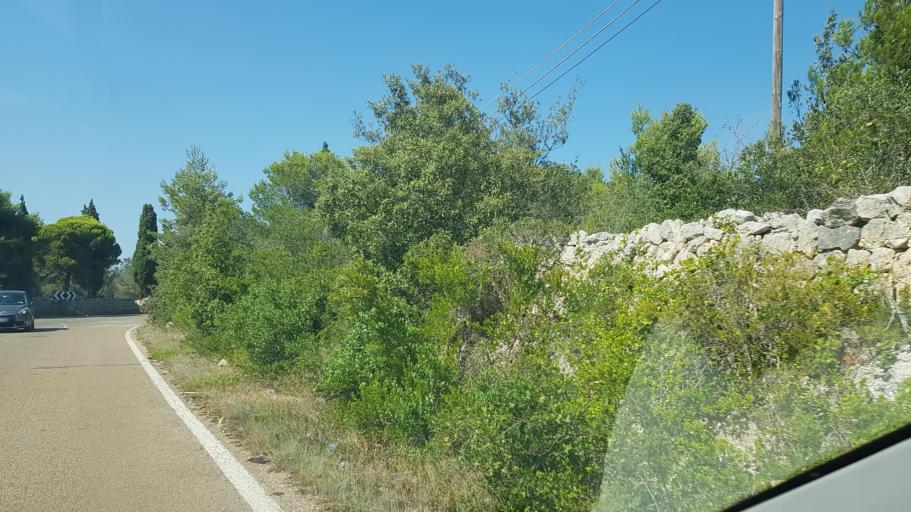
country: IT
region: Apulia
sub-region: Provincia di Lecce
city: Gemini
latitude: 39.8590
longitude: 18.2041
